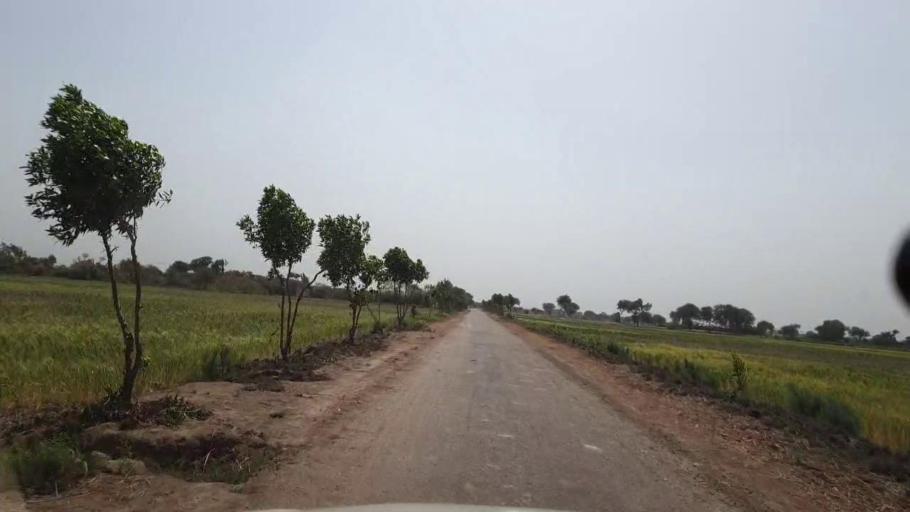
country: PK
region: Sindh
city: Matli
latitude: 25.0438
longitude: 68.6857
